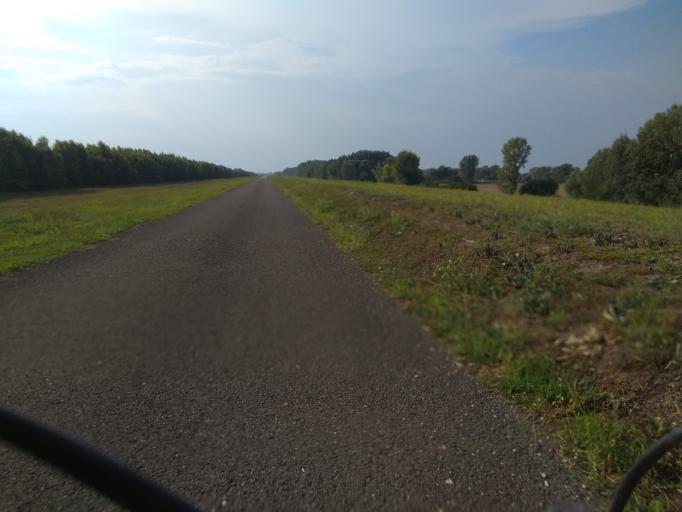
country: SK
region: Trnavsky
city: Gabcikovo
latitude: 47.8415
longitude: 17.5880
